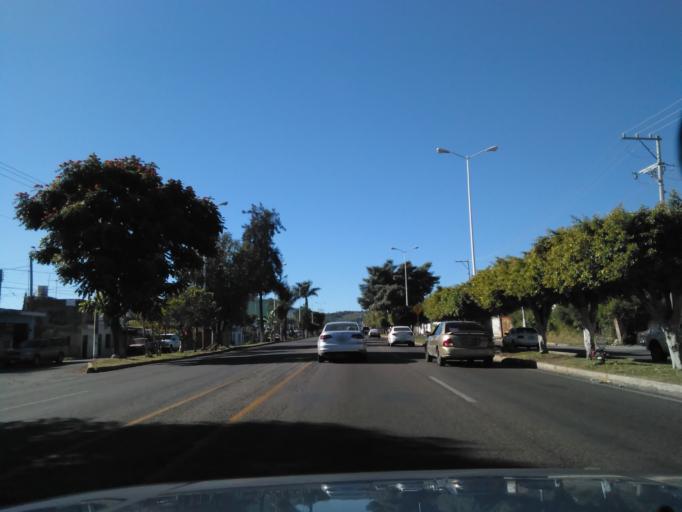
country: MX
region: Nayarit
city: Xalisco
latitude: 21.4539
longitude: -104.8972
